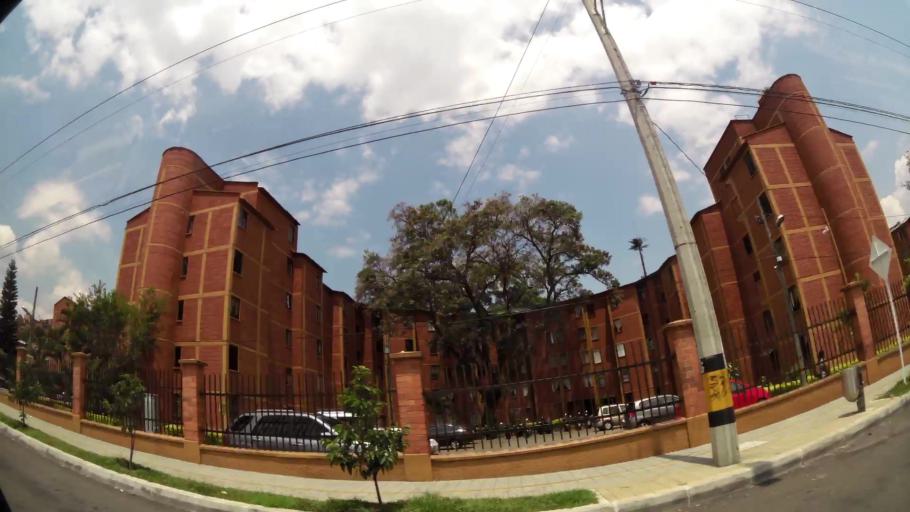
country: CO
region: Antioquia
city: Itagui
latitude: 6.1769
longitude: -75.6051
